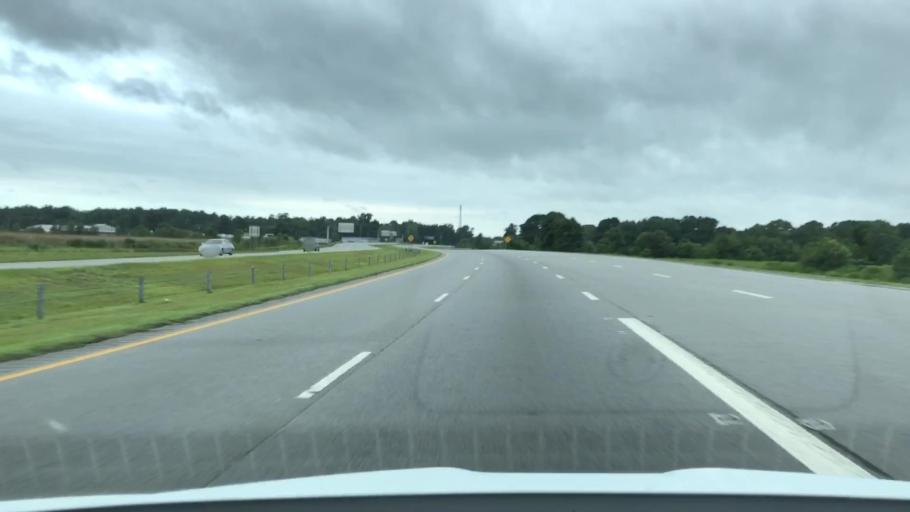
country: US
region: North Carolina
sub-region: Lenoir County
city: Kinston
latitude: 35.2649
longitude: -77.6826
